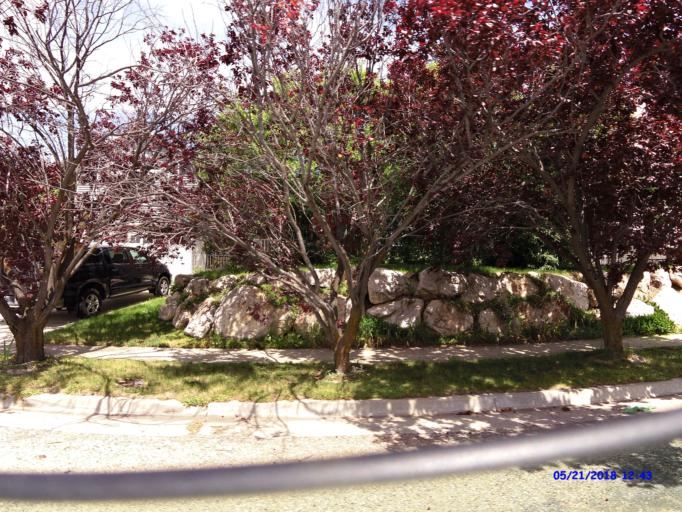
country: US
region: Utah
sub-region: Weber County
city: Washington Terrace
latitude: 41.1721
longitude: -111.9504
